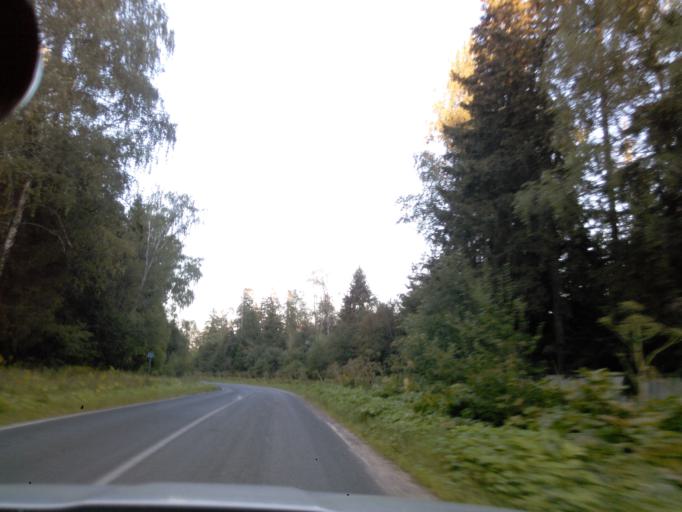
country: RU
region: Moskovskaya
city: Solnechnogorsk
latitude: 56.1276
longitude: 36.8642
